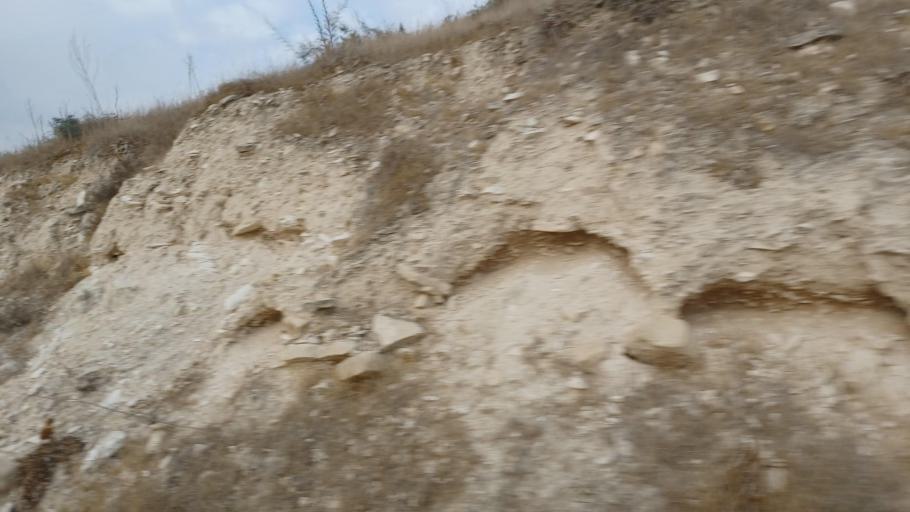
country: CY
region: Larnaka
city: Troulloi
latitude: 35.0272
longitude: 33.5744
